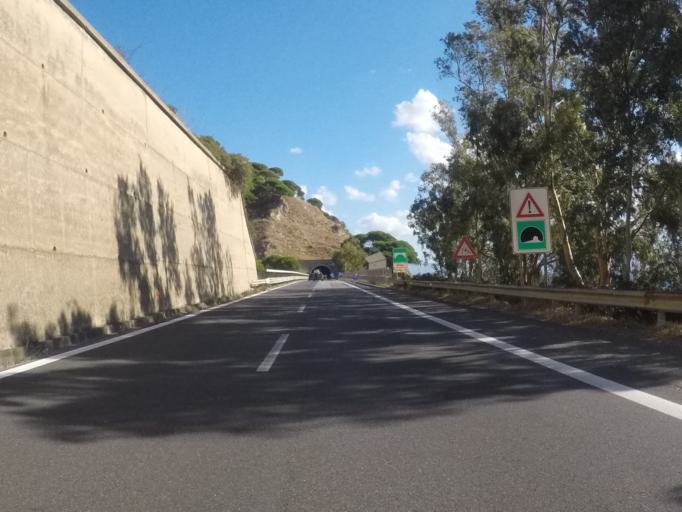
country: IT
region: Sicily
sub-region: Messina
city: Scaletta Zanclea
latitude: 38.0700
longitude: 15.4862
